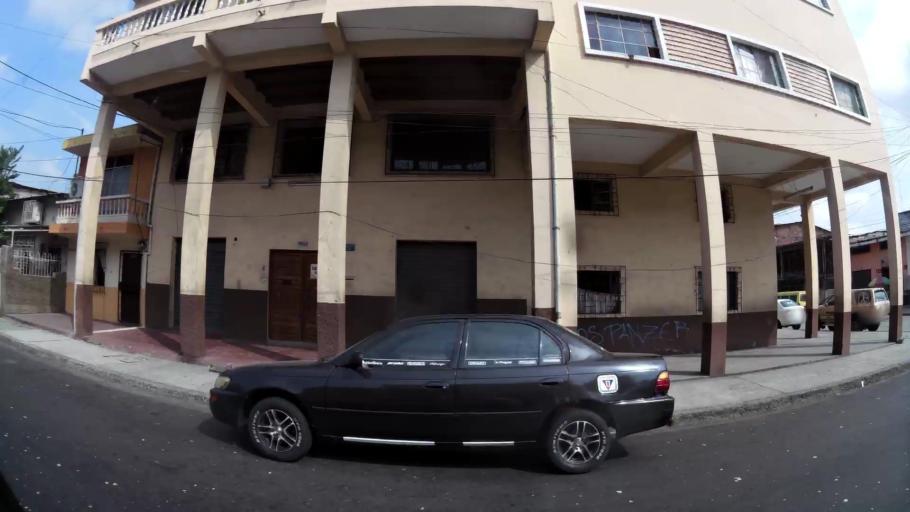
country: EC
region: Guayas
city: Guayaquil
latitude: -2.2027
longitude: -79.9011
